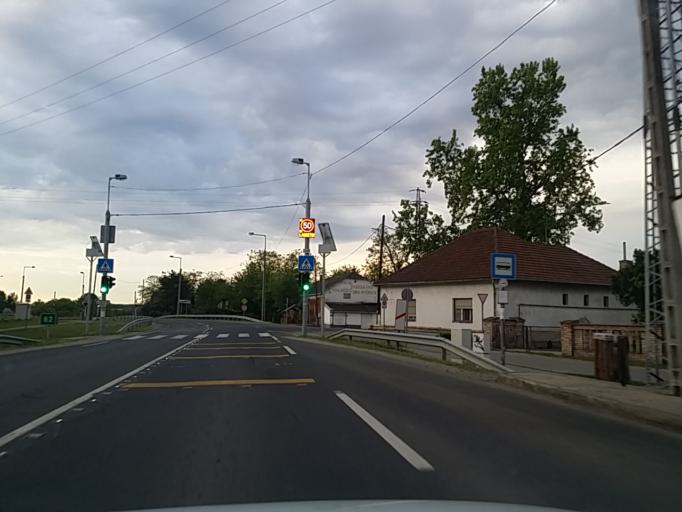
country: HU
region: Pest
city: Taborfalva
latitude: 47.0688
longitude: 19.4982
